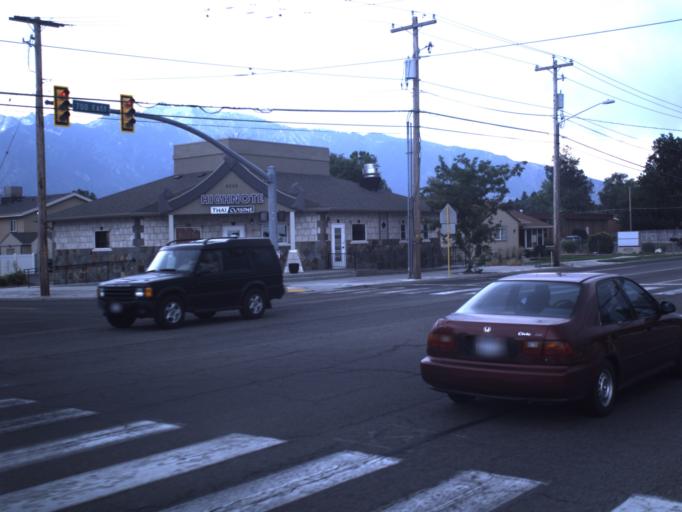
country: US
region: Utah
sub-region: Salt Lake County
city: Sandy City
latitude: 40.6060
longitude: -111.8723
